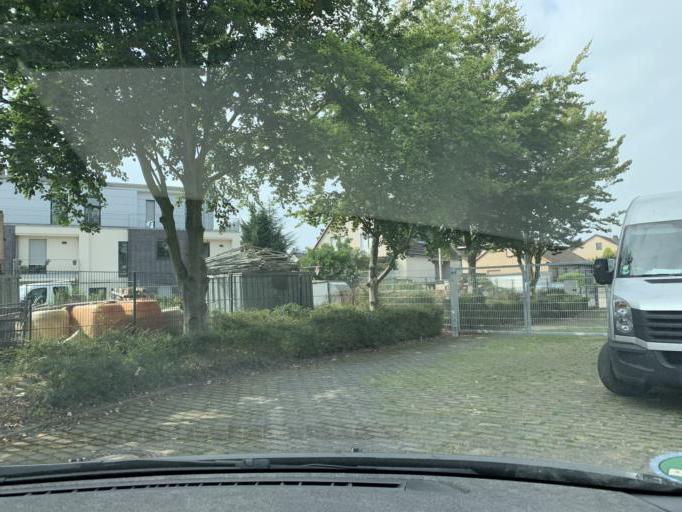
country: DE
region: North Rhine-Westphalia
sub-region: Regierungsbezirk Koln
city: Erftstadt
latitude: 50.7999
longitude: 6.7590
